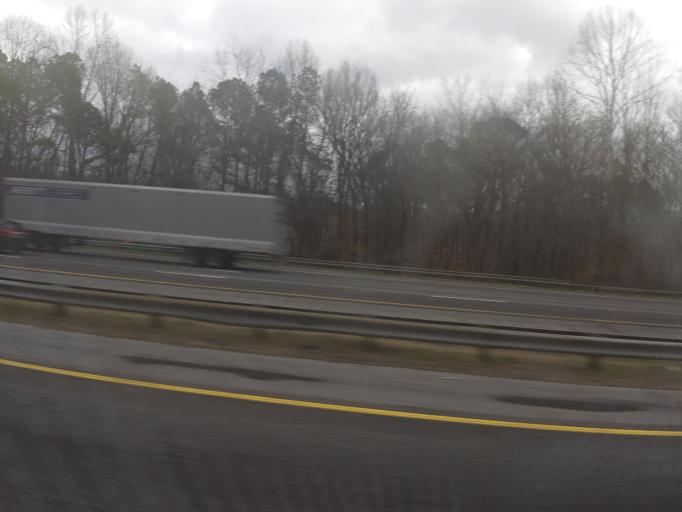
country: US
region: Georgia
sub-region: Whitfield County
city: Dalton
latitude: 34.7836
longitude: -85.0006
